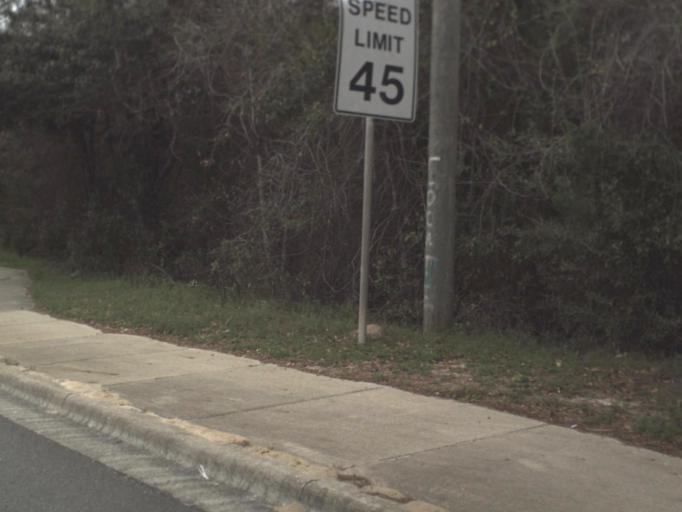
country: US
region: Florida
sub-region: Leon County
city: Tallahassee
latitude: 30.5594
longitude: -84.2192
